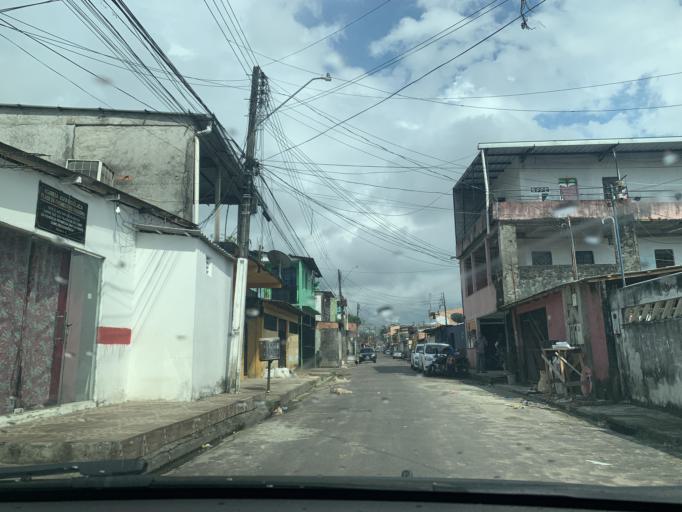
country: BR
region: Amazonas
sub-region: Manaus
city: Manaus
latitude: -3.0831
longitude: -59.9650
